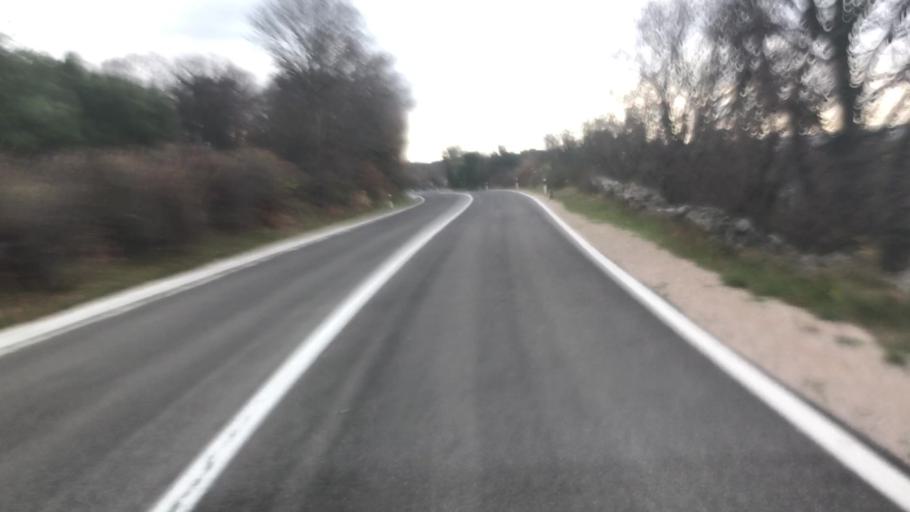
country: HR
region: Zadarska
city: Razanac
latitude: 44.3424
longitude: 15.3346
